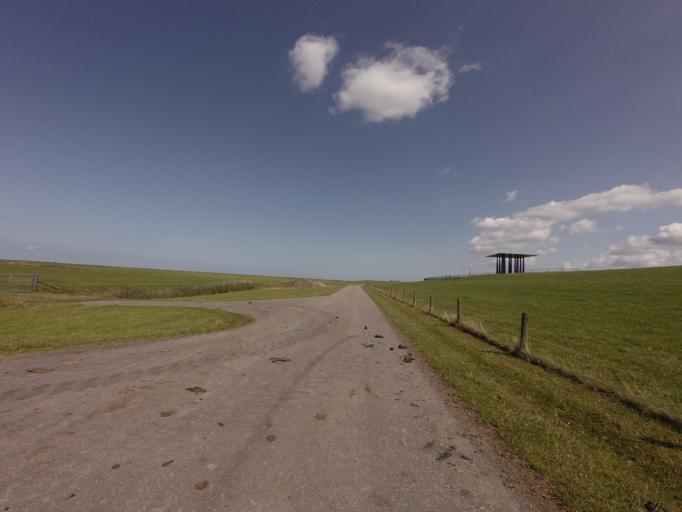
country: NL
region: Friesland
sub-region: Gemeente Ferwerderadiel
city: Hallum
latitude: 53.3317
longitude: 5.7754
